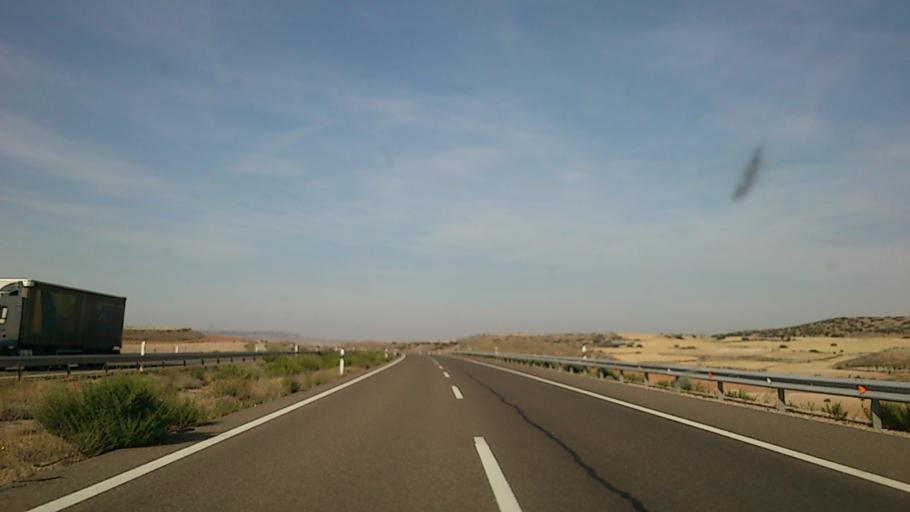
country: ES
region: Aragon
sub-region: Provincia de Zaragoza
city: Longares
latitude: 41.4209
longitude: -1.1542
